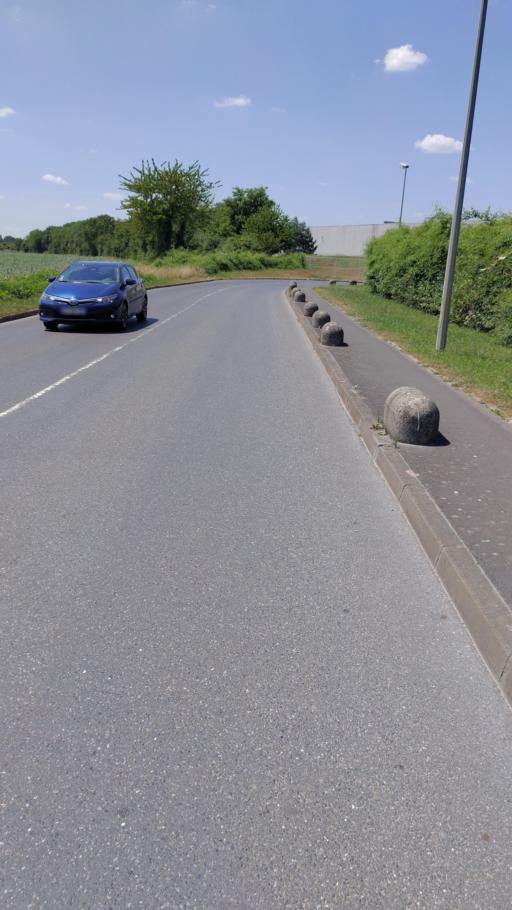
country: FR
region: Ile-de-France
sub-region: Departement du Val-de-Marne
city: Santeny
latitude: 48.7149
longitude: 2.5717
